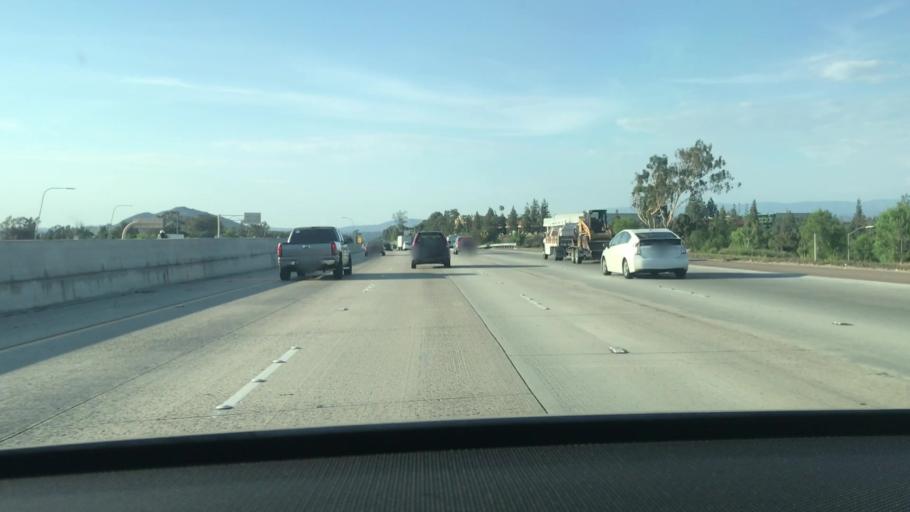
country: US
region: California
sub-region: San Diego County
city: Poway
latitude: 33.0208
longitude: -117.0784
